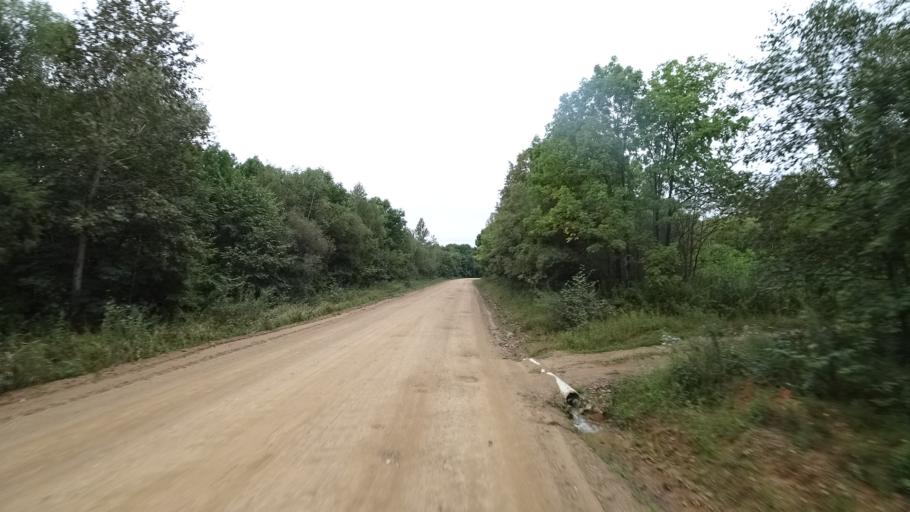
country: RU
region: Primorskiy
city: Rettikhovka
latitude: 44.1817
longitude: 132.8048
